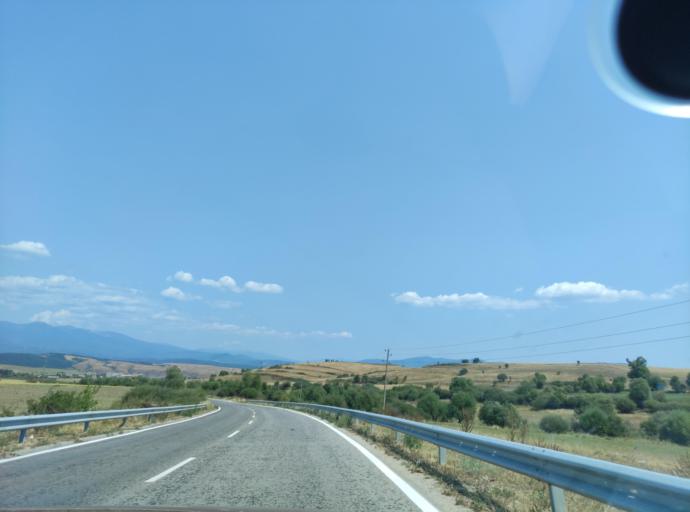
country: BG
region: Blagoevgrad
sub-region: Obshtina Razlog
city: Razlog
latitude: 41.8719
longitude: 23.4784
